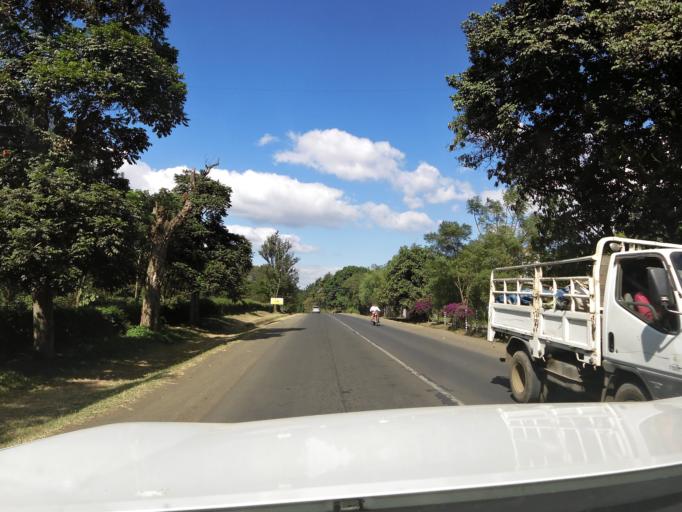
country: TZ
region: Arusha
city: Arusha
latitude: -3.3762
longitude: 36.6501
